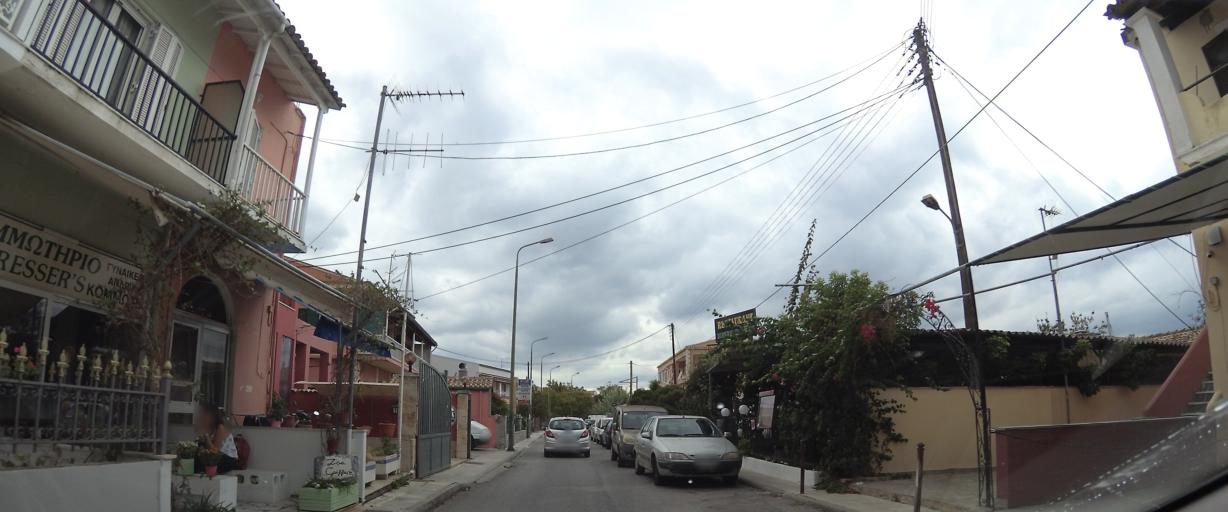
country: GR
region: Ionian Islands
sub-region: Nomos Kerkyras
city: Kontokali
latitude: 39.6459
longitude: 19.8506
